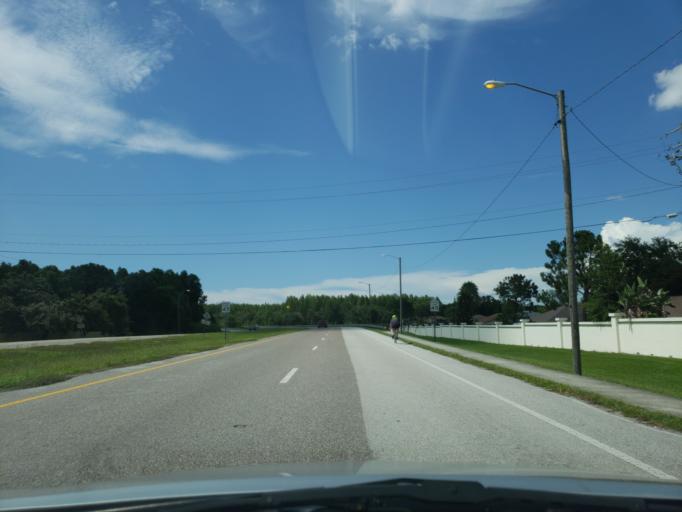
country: US
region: Florida
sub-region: Hillsborough County
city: Carrollwood Village
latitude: 28.0485
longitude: -82.5419
